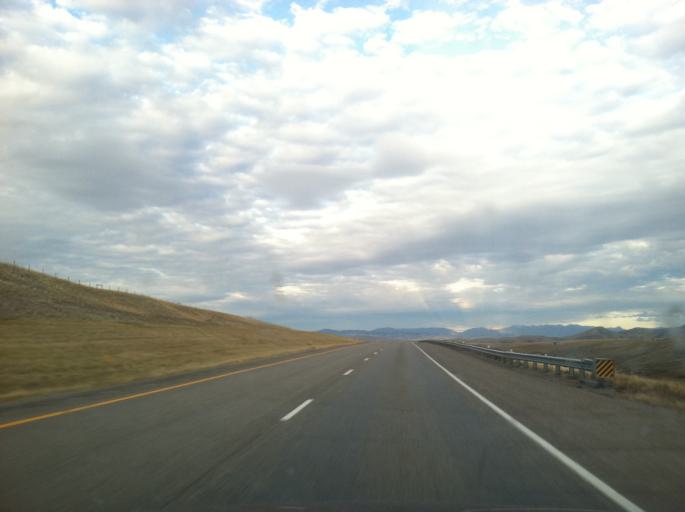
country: US
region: Montana
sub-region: Gallatin County
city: Three Forks
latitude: 45.9089
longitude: -111.7901
